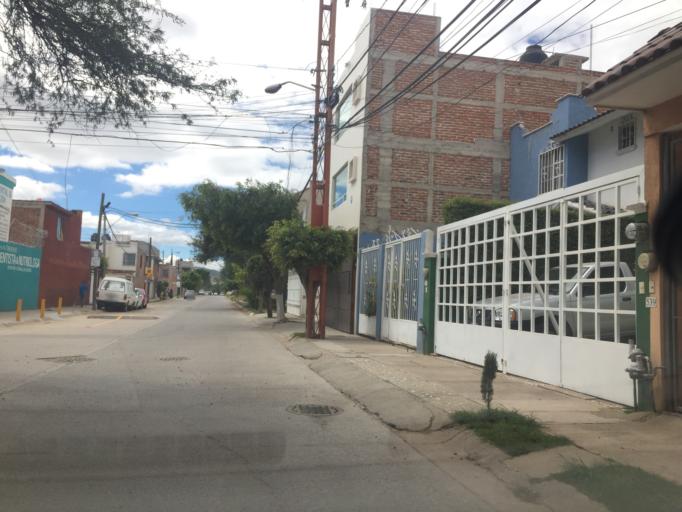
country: MX
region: Guanajuato
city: Leon
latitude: 21.1534
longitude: -101.6560
